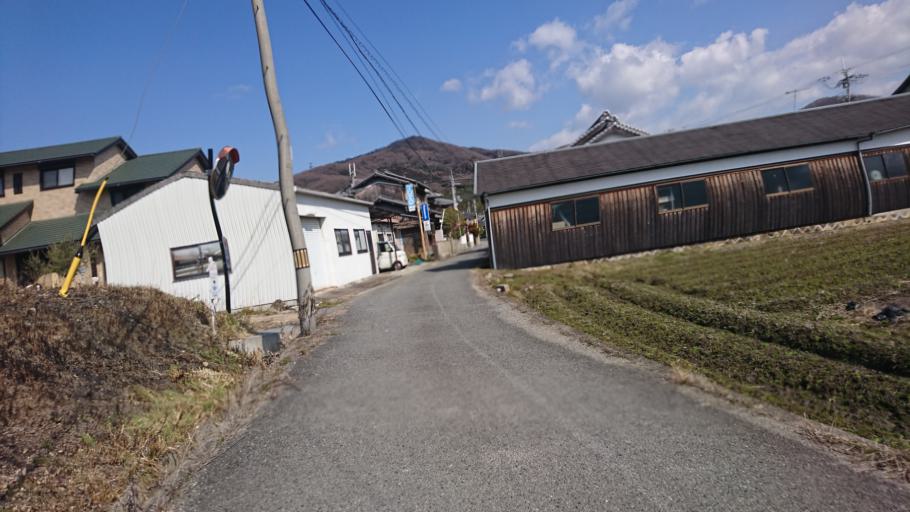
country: JP
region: Hyogo
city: Kakogawacho-honmachi
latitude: 34.8235
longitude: 134.8028
